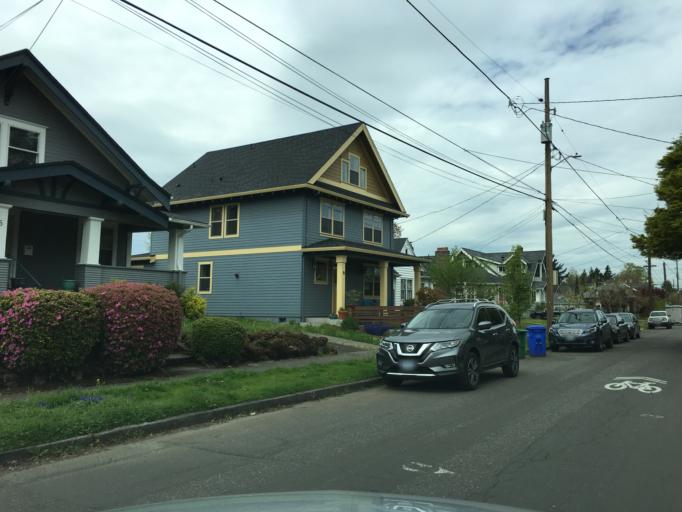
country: US
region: Oregon
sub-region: Multnomah County
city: Lents
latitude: 45.5232
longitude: -122.5899
